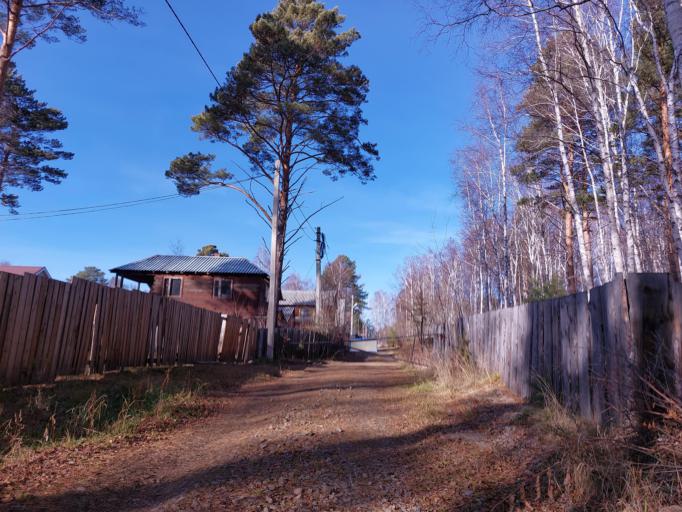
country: RU
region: Irkutsk
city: Pivovarikha
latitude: 52.1856
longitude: 104.4559
